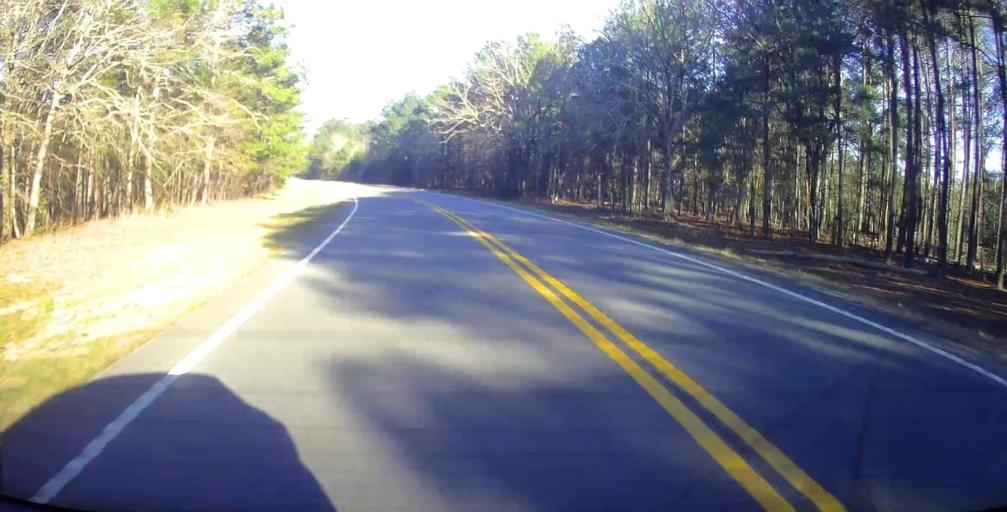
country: US
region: Georgia
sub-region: Taylor County
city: Butler
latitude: 32.4754
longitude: -84.3844
